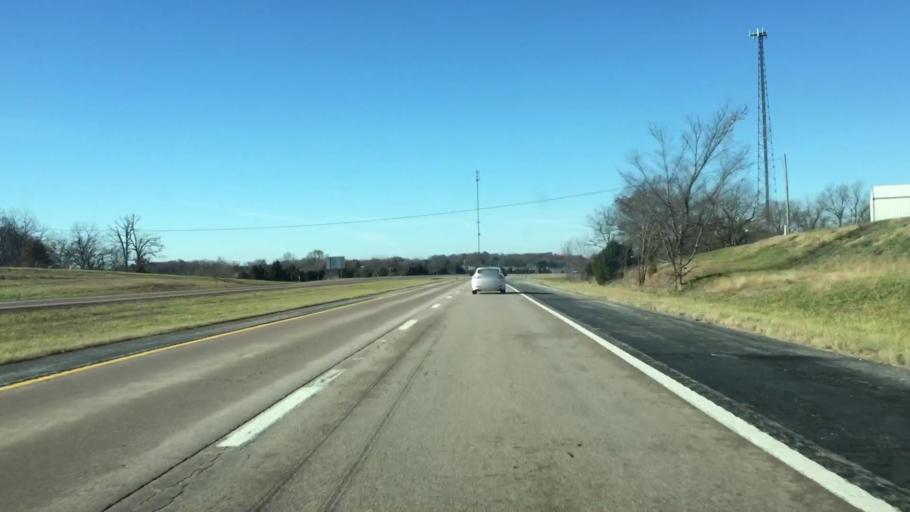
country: US
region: Missouri
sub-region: Miller County
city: Tuscumbia
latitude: 38.3748
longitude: -92.4100
